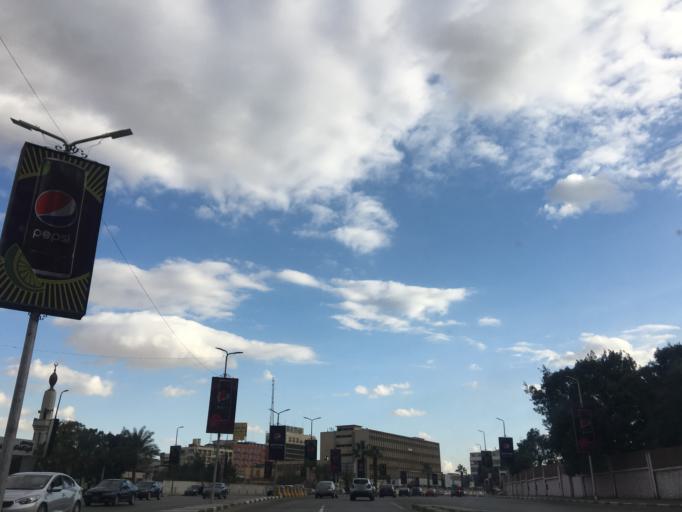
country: EG
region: Muhafazat al Qahirah
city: Cairo
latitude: 30.0564
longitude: 31.3060
